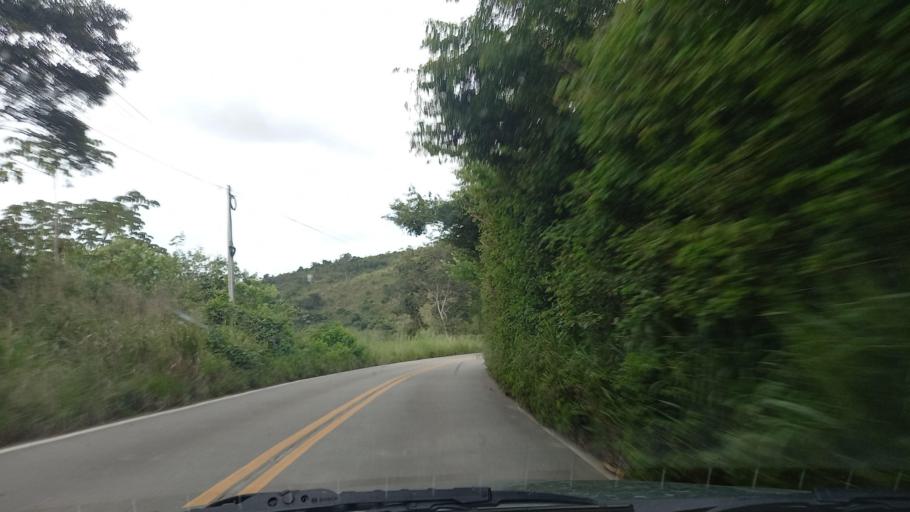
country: BR
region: Pernambuco
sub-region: Maraial
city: Maraial
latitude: -8.7687
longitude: -35.8656
